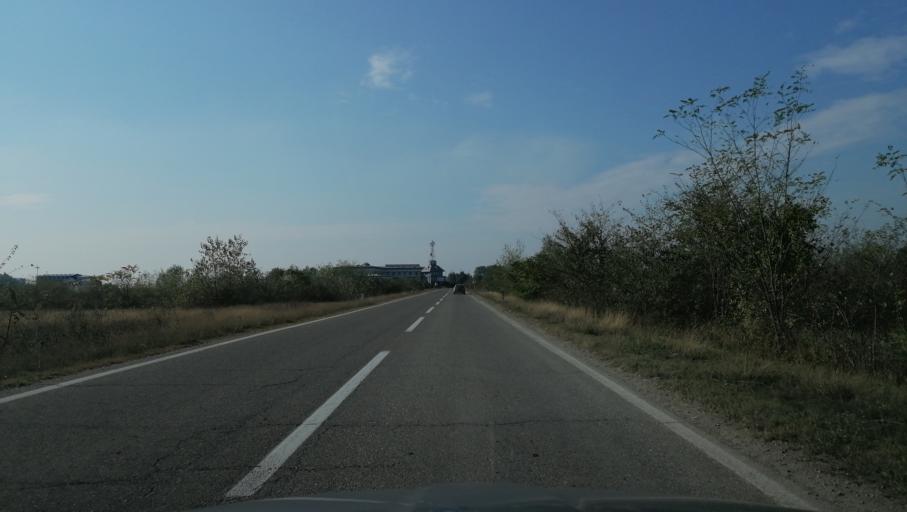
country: BA
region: Republika Srpska
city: Popovi
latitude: 44.7777
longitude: 19.3238
